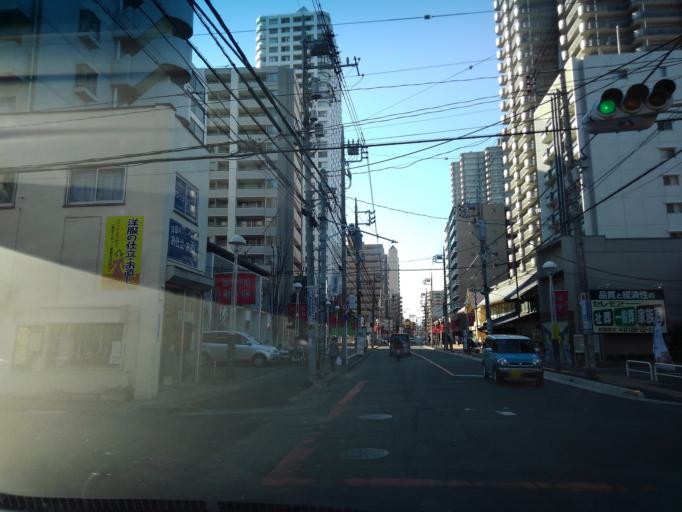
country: JP
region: Saitama
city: Tokorozawa
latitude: 35.7912
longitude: 139.4686
